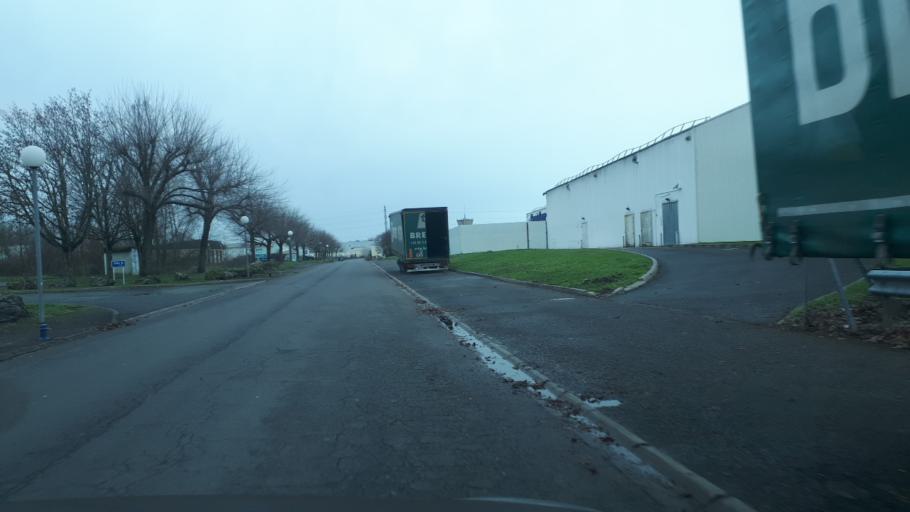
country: FR
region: Centre
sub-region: Departement du Loir-et-Cher
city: Romorantin-Lanthenay
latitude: 47.3366
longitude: 1.7477
